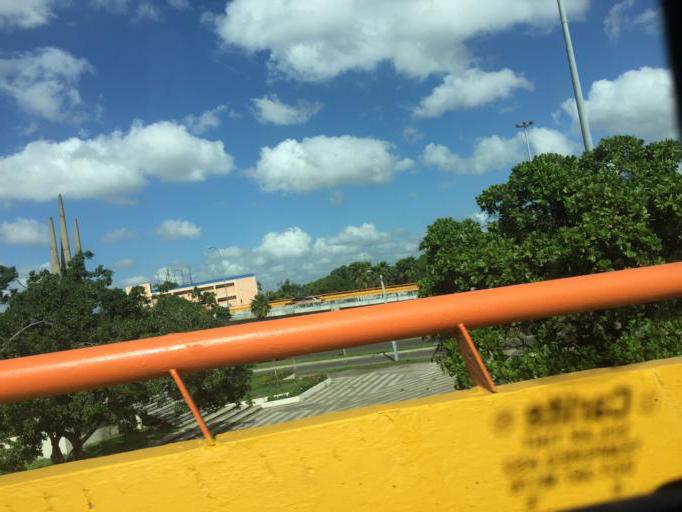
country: DO
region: Nacional
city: San Carlos
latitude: 18.4862
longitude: -69.8881
